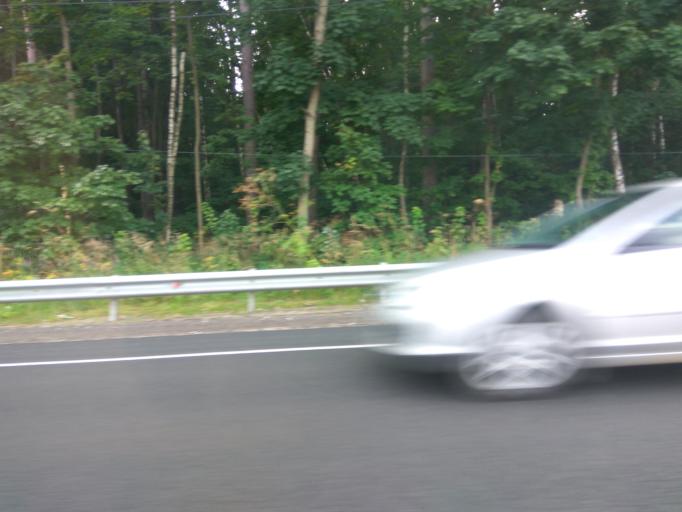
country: RU
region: Moskovskaya
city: Udel'naya
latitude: 55.6245
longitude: 38.0153
